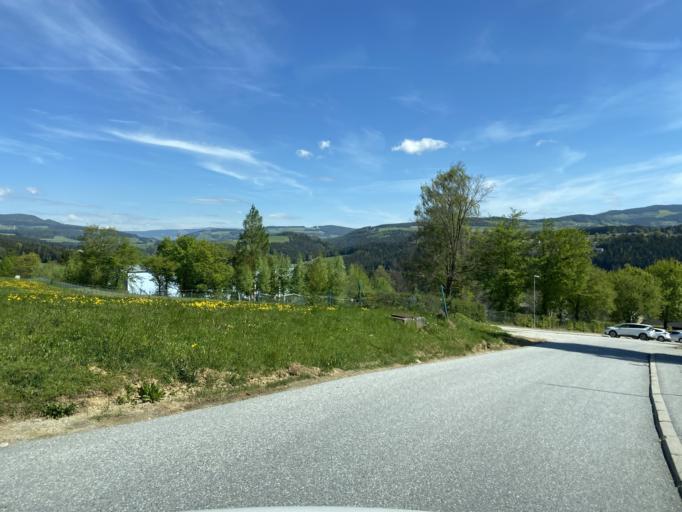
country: AT
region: Styria
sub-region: Politischer Bezirk Weiz
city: Birkfeld
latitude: 47.3516
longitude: 15.6902
